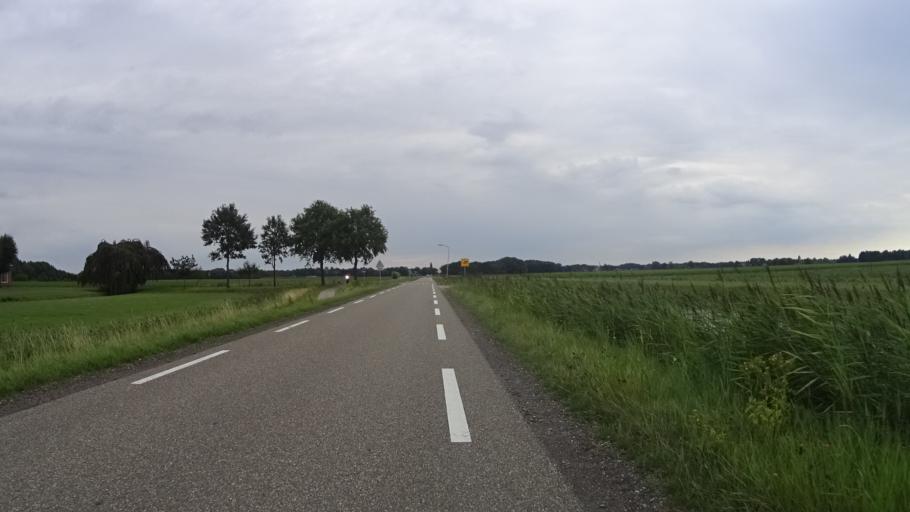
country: NL
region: Groningen
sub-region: Gemeente Slochteren
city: Slochteren
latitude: 53.2263
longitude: 6.7808
